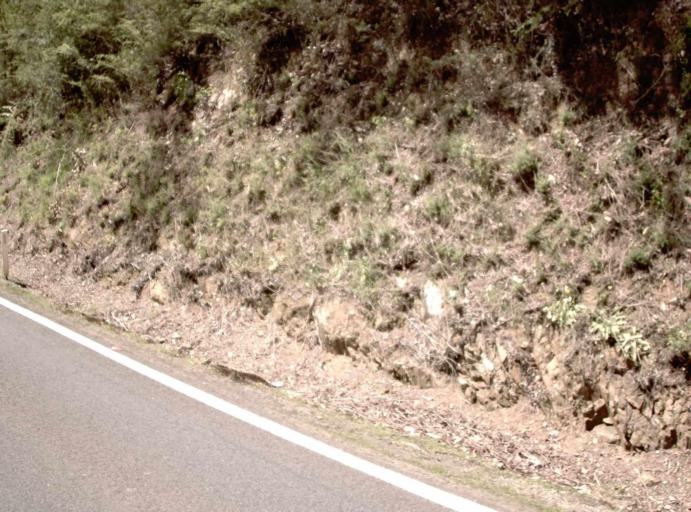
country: AU
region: New South Wales
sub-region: Bombala
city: Bombala
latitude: -37.5891
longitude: 148.9186
